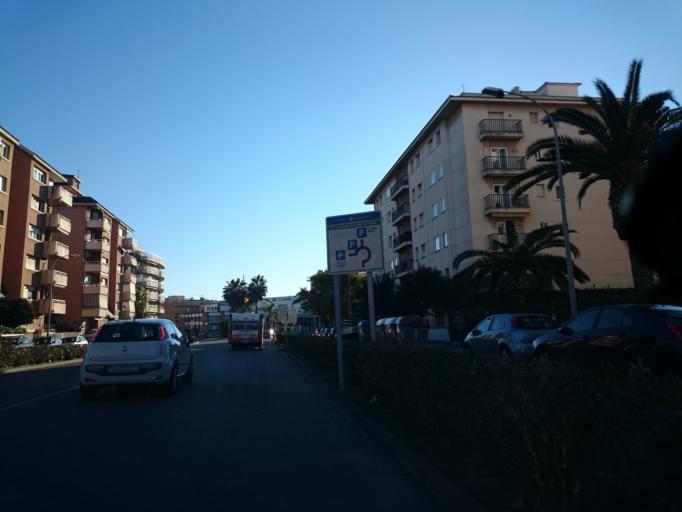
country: ES
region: Catalonia
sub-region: Provincia de Barcelona
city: Vilanova i la Geltru
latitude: 41.2197
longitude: 1.7201
